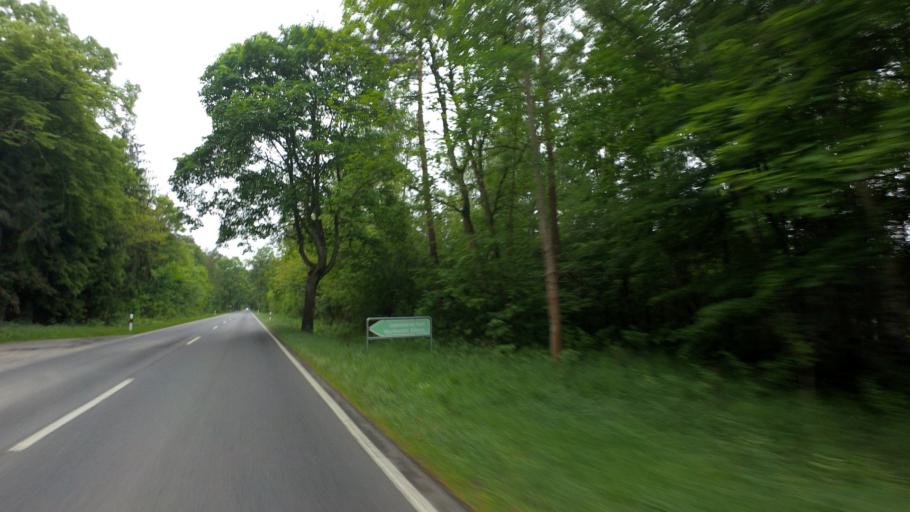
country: DE
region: Brandenburg
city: Friedrichswalde
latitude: 52.9947
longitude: 13.5920
